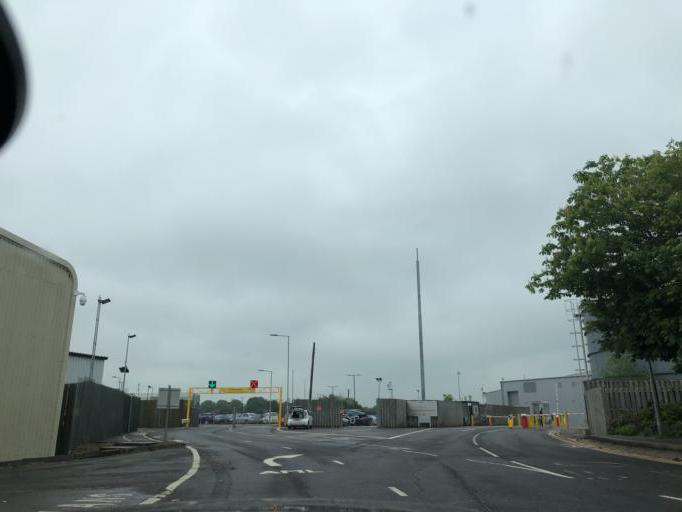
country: GB
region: England
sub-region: Warwickshire
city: Harbury
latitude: 52.1938
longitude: -1.4871
